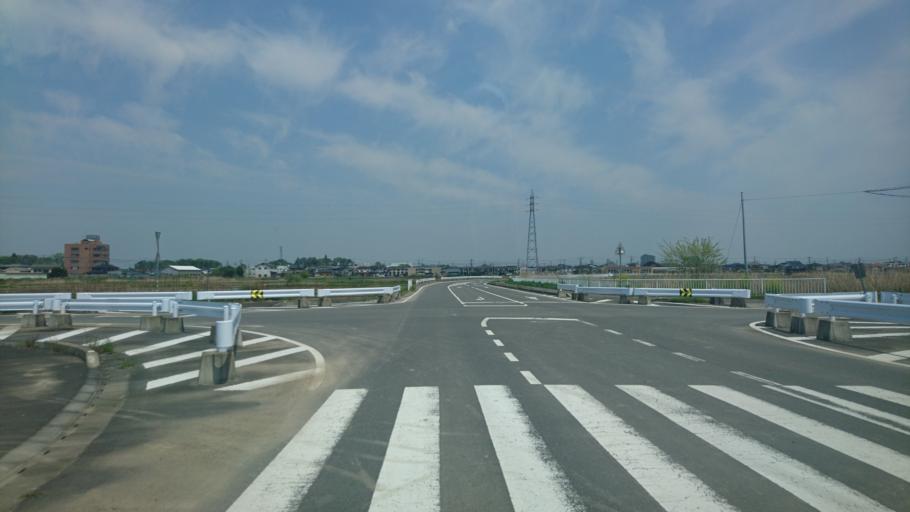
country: JP
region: Ibaraki
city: Mitsukaido
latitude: 36.0076
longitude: 139.9840
